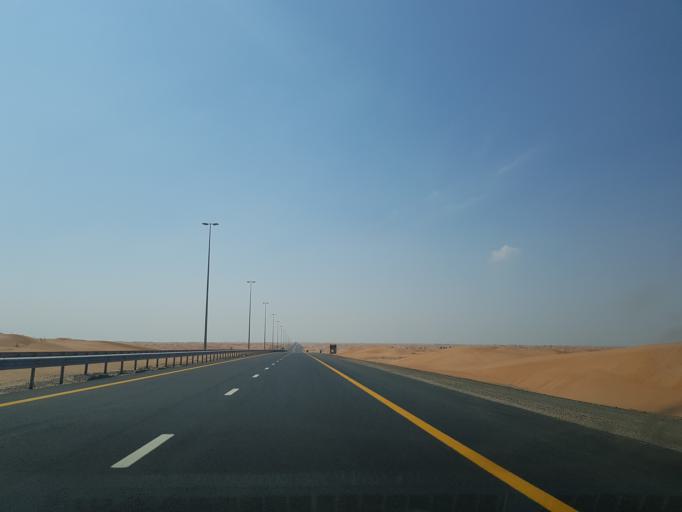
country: AE
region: Ash Shariqah
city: Adh Dhayd
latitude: 25.2503
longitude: 55.8025
